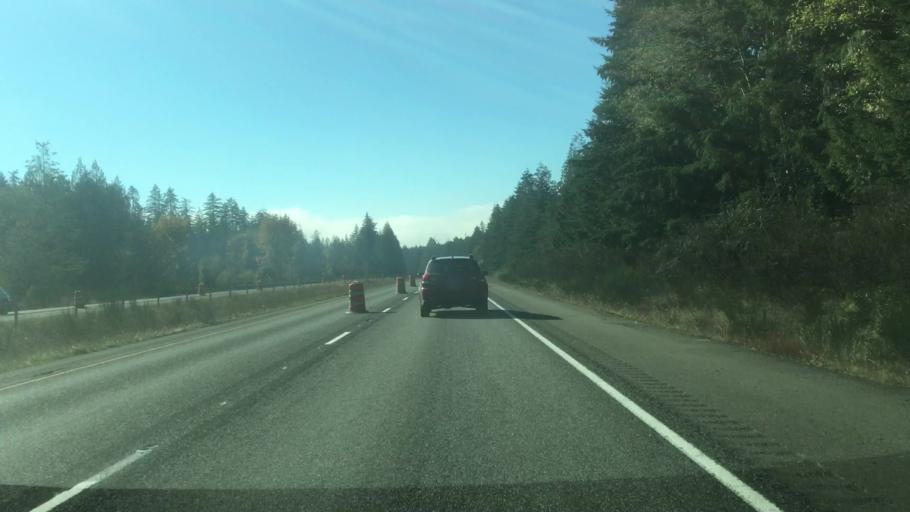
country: US
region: Washington
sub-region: Grays Harbor County
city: McCleary
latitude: 47.0506
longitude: -123.3008
